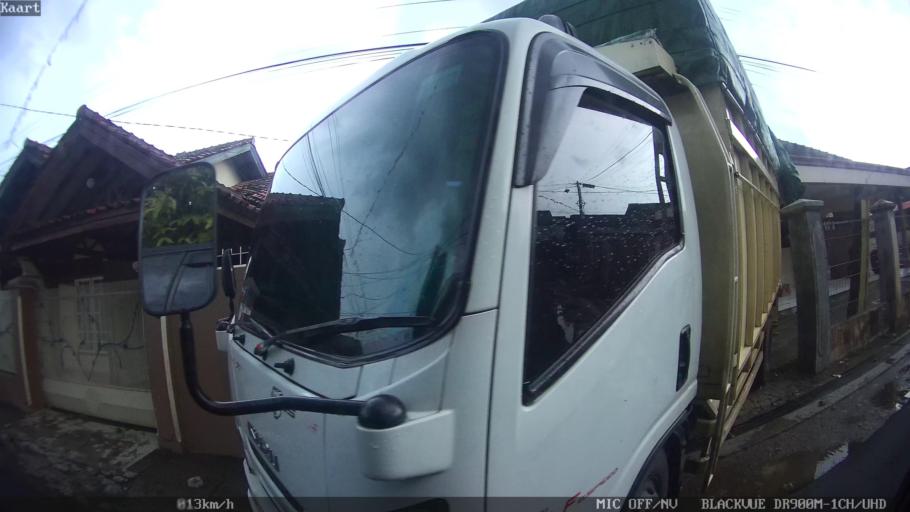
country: ID
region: Lampung
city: Kedaton
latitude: -5.3970
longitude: 105.2849
